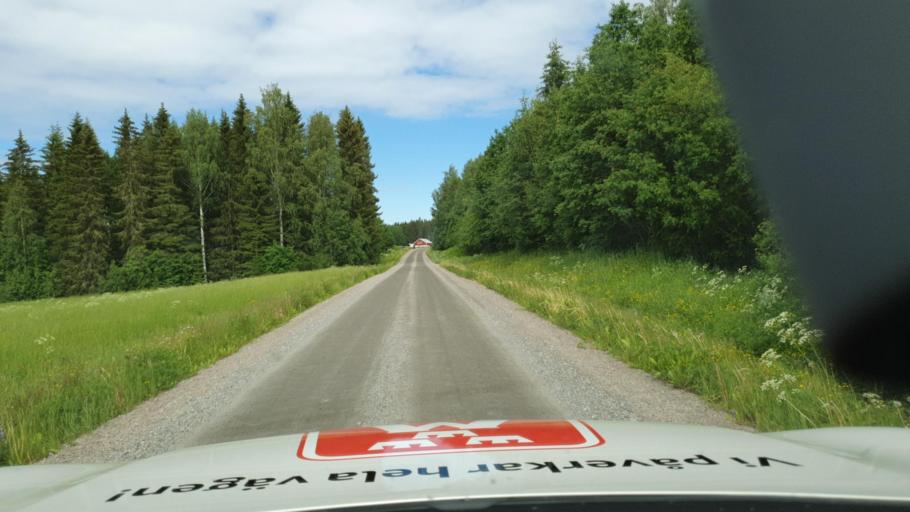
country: SE
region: Vaesterbotten
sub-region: Skelleftea Kommun
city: Forsbacka
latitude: 64.6341
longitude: 20.5481
